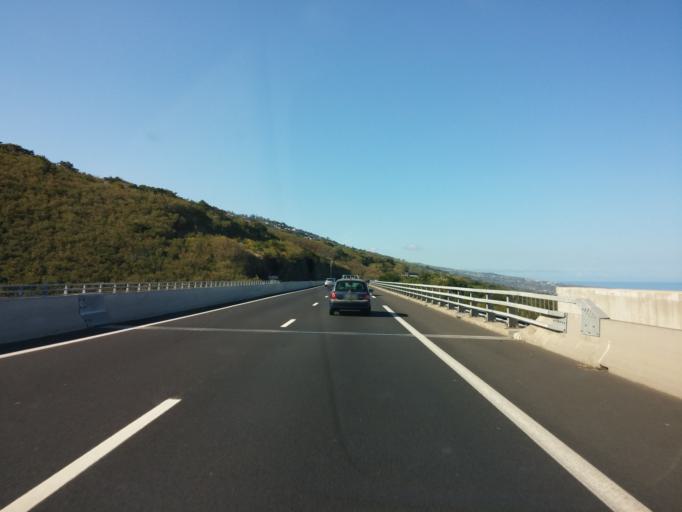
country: RE
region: Reunion
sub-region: Reunion
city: Trois-Bassins
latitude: -21.1177
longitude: 55.2775
